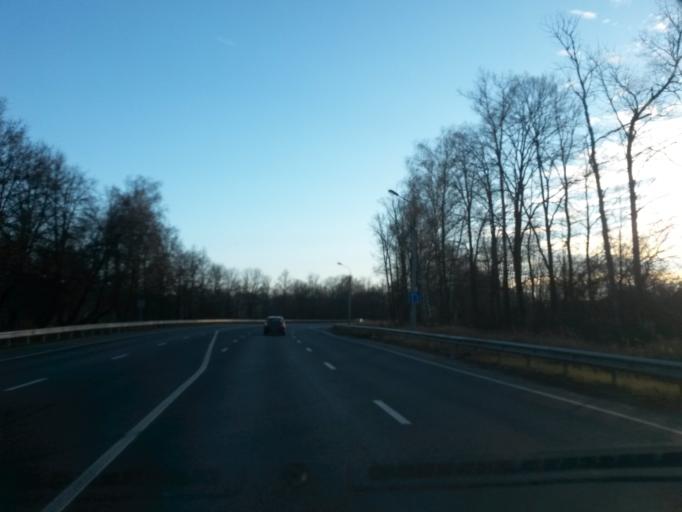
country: RU
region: Moskovskaya
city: L'vovskiy
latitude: 55.3035
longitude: 37.5288
